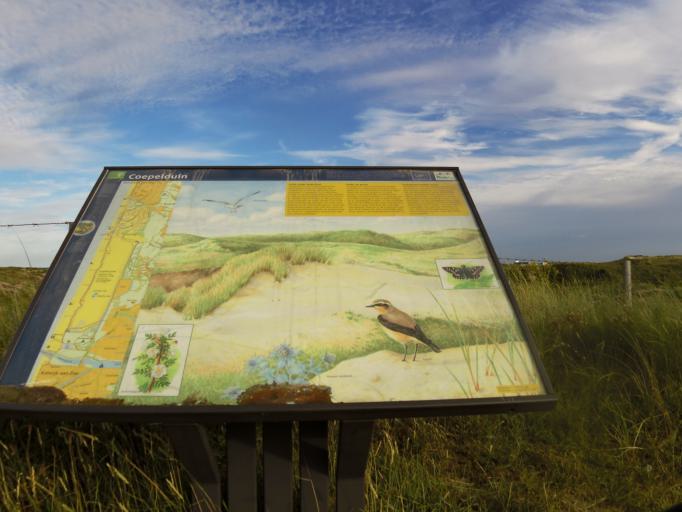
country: NL
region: South Holland
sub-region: Gemeente Noordwijk
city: Noordwijk-Binnen
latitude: 52.2296
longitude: 4.4183
